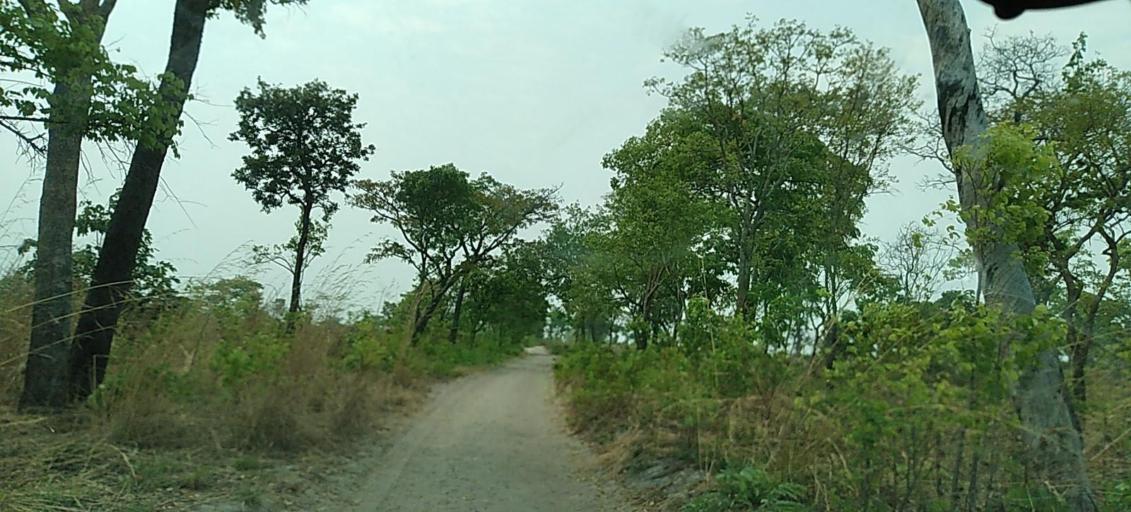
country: ZM
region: North-Western
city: Kabompo
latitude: -13.4695
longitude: 24.4444
